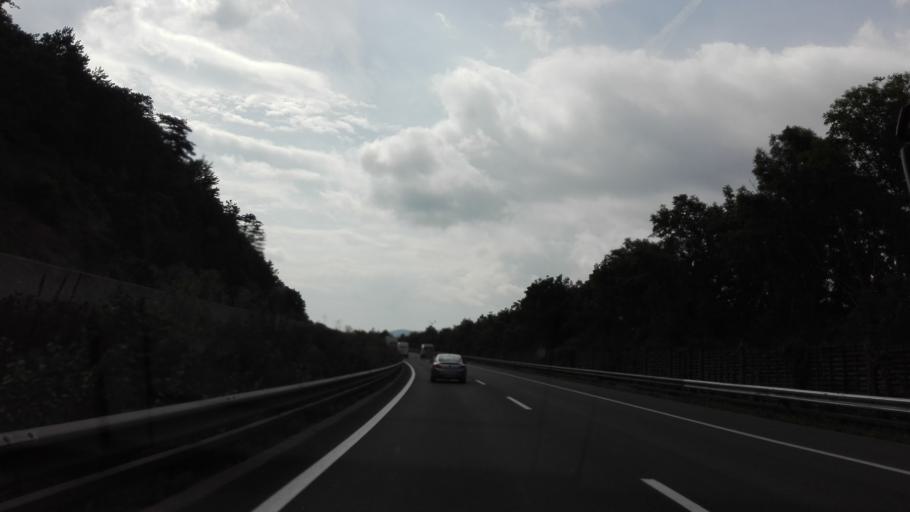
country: AT
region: Lower Austria
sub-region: Politischer Bezirk Baden
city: Alland
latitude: 48.0648
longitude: 16.0696
